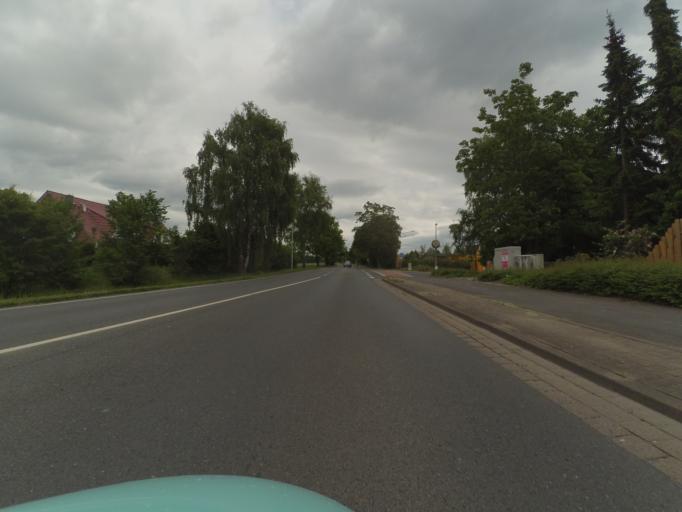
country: DE
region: Lower Saxony
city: Garbsen
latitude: 52.4409
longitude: 9.5500
